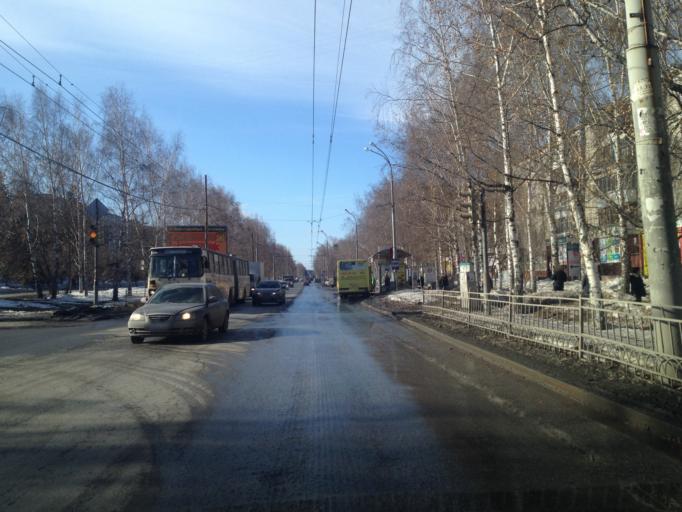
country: RU
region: Sverdlovsk
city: Sovkhoznyy
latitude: 56.7995
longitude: 60.5746
